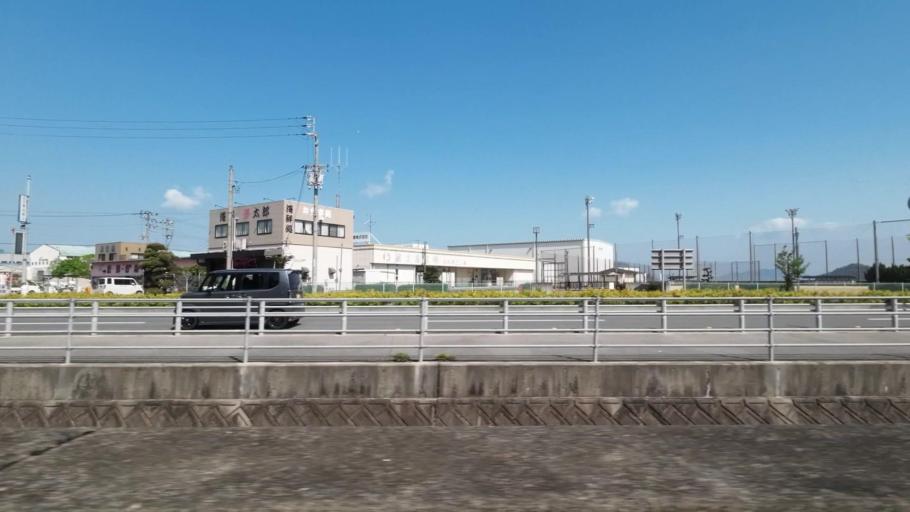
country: JP
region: Kagawa
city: Tadotsu
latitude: 34.2333
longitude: 133.6975
